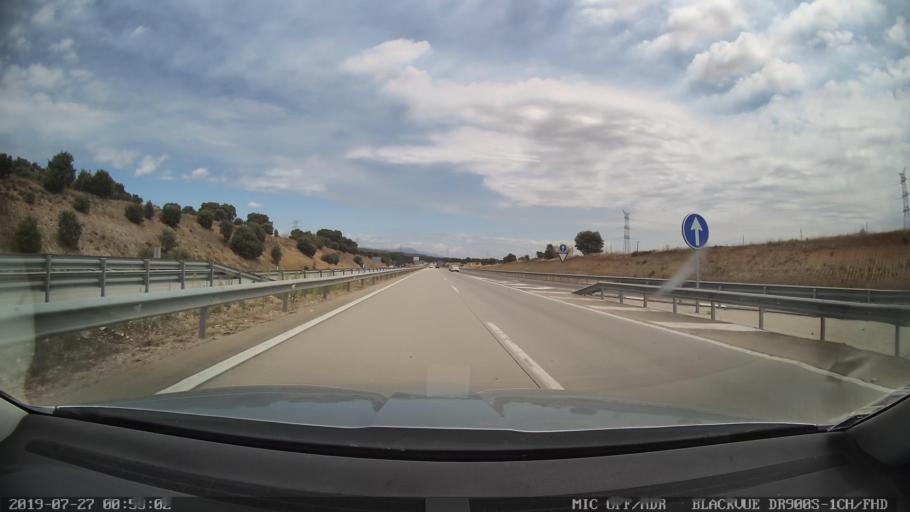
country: ES
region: Castille-La Mancha
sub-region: Province of Toledo
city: Mejorada
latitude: 39.9630
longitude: -4.9011
